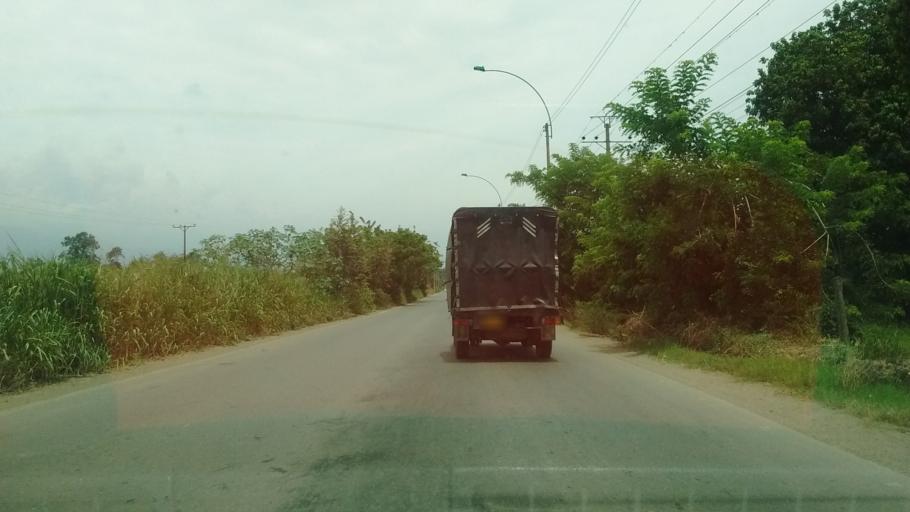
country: CO
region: Valle del Cauca
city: Jamundi
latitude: 3.3075
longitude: -76.4824
